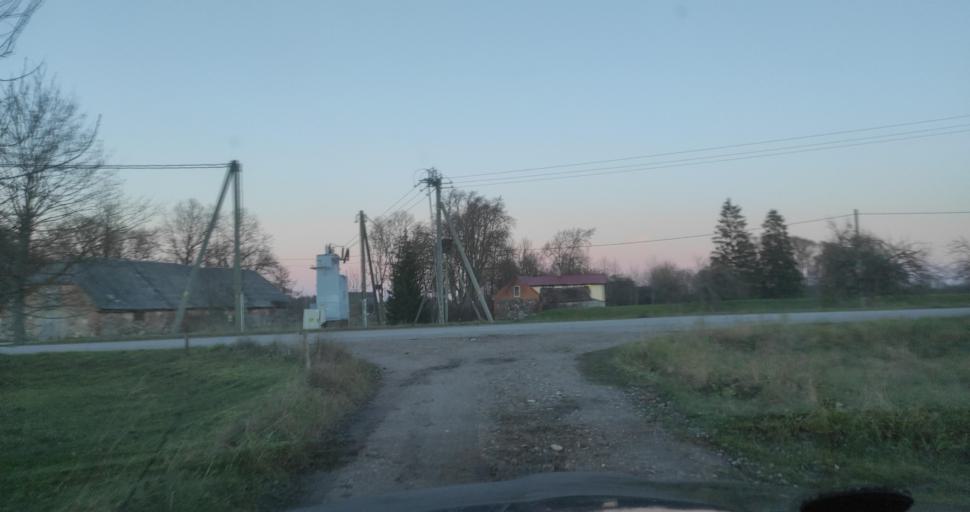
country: LV
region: Dundaga
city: Dundaga
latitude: 57.3750
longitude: 22.2299
